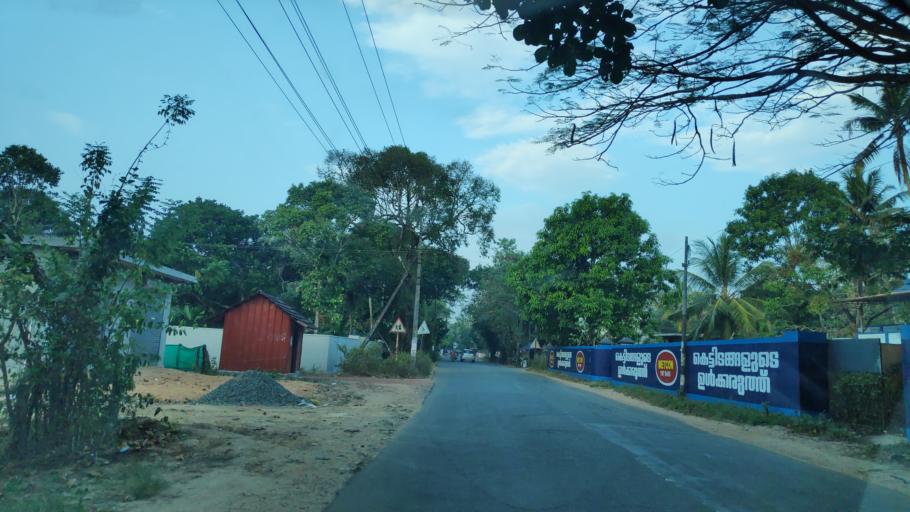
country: IN
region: Kerala
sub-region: Alappuzha
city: Shertallai
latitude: 9.6271
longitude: 76.3684
